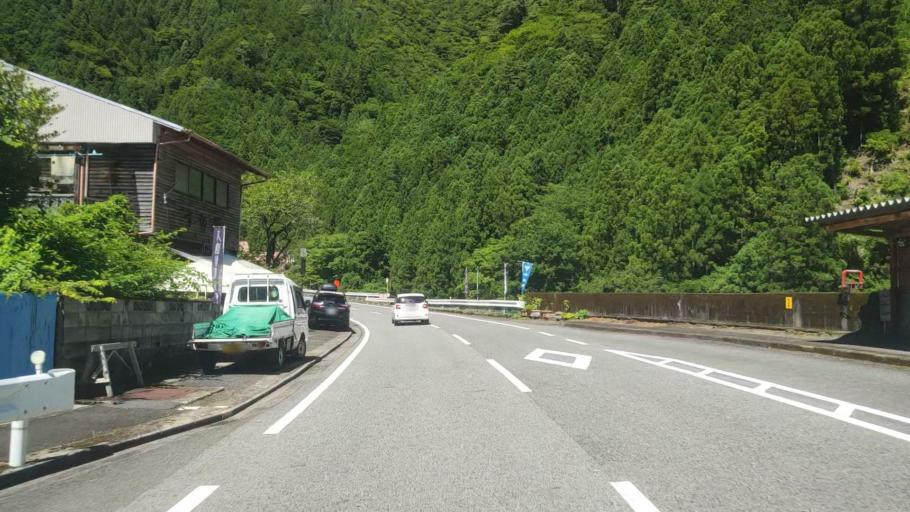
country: JP
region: Mie
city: Owase
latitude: 34.1812
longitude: 136.0061
